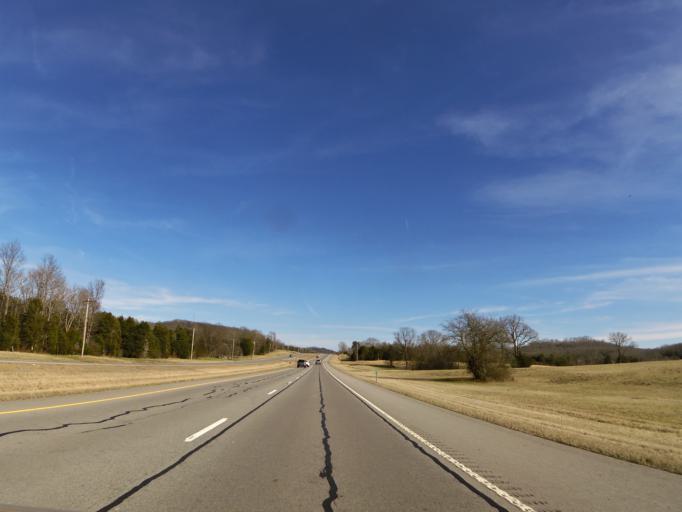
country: US
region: Tennessee
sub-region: Cannon County
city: Woodbury
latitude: 35.8164
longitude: -86.2263
